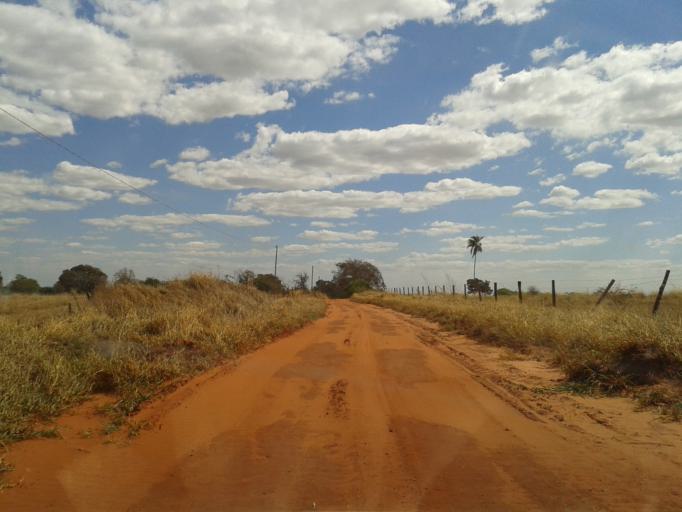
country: BR
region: Minas Gerais
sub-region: Monte Alegre De Minas
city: Monte Alegre de Minas
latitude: -18.7767
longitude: -49.0830
